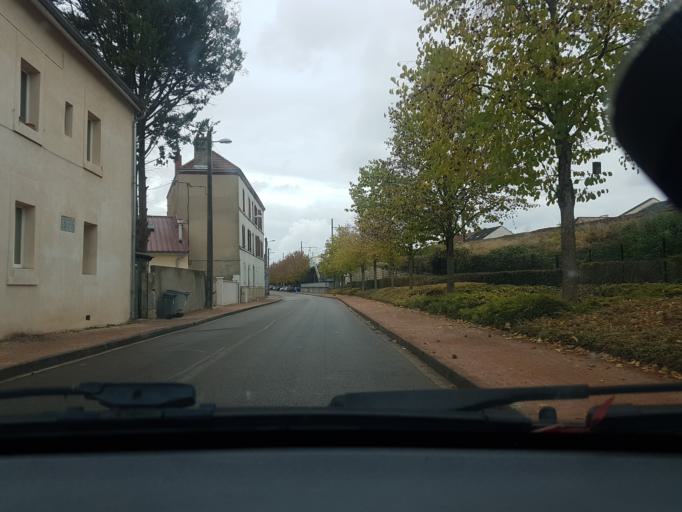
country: FR
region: Bourgogne
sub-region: Departement de la Cote-d'Or
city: Saint-Apollinaire
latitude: 47.3238
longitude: 5.0560
